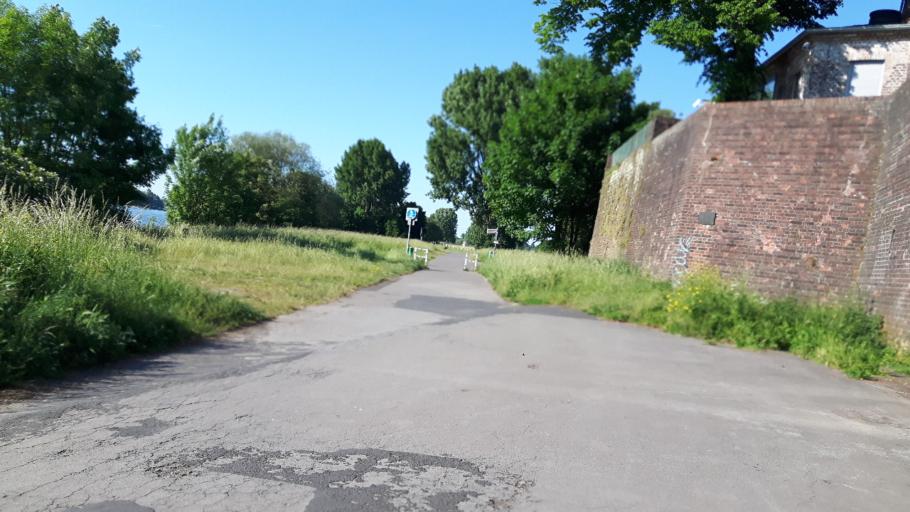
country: DE
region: North Rhine-Westphalia
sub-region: Regierungsbezirk Dusseldorf
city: Meerbusch
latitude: 51.3027
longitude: 6.7343
